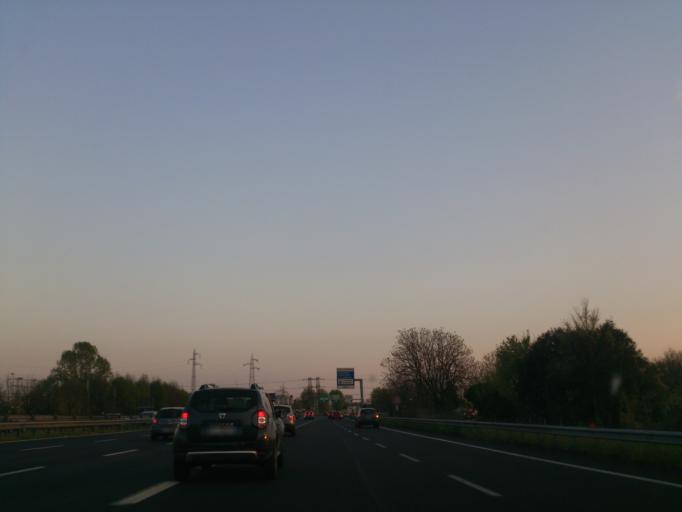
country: IT
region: Lombardy
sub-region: Citta metropolitana di Milano
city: Cologno Monzese
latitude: 45.5196
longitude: 9.2611
